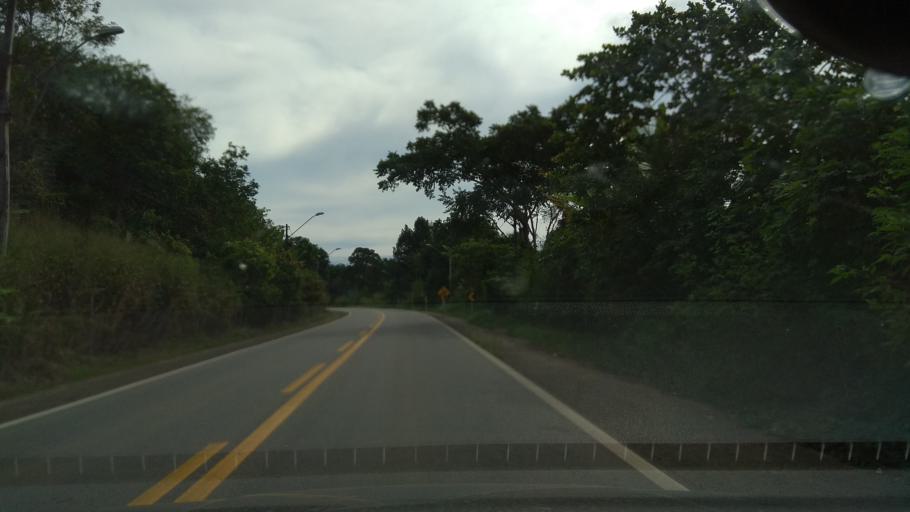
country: BR
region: Bahia
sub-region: Ubata
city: Ubata
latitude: -14.1944
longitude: -39.5477
